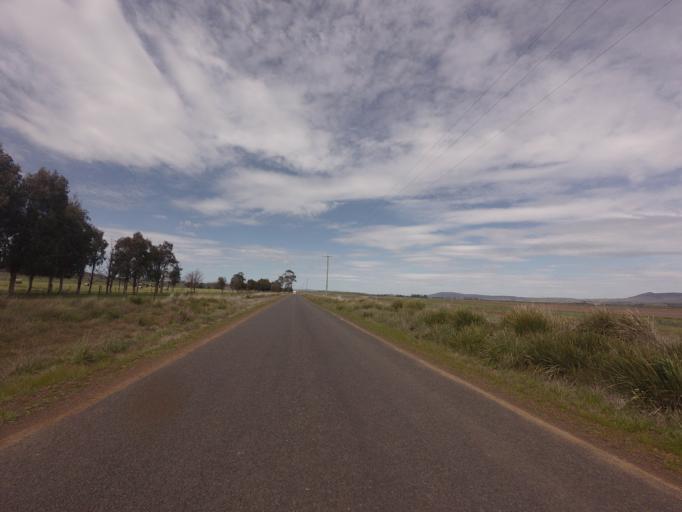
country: AU
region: Tasmania
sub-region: Northern Midlands
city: Evandale
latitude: -41.8166
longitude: 147.3000
